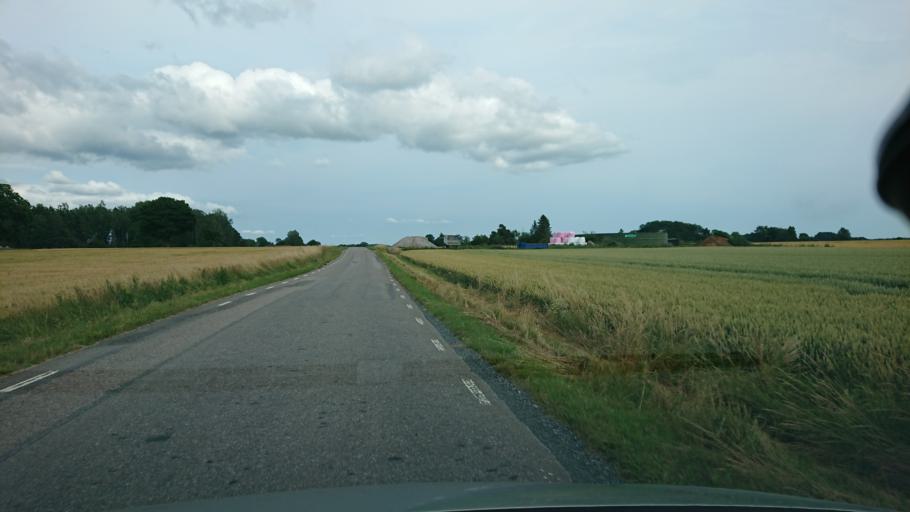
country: SE
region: Uppsala
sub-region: Osthammars Kommun
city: Bjorklinge
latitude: 59.9903
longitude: 17.5193
